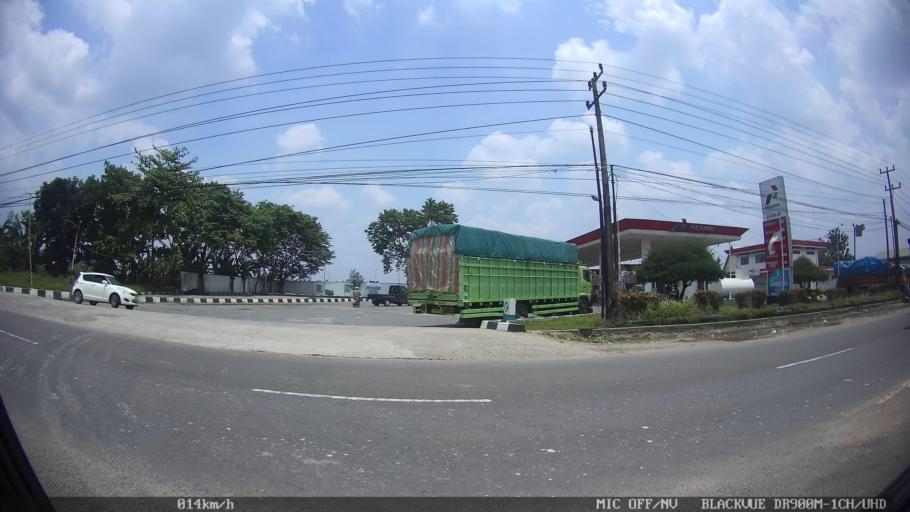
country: ID
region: Lampung
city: Natar
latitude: -5.2984
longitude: 105.1921
